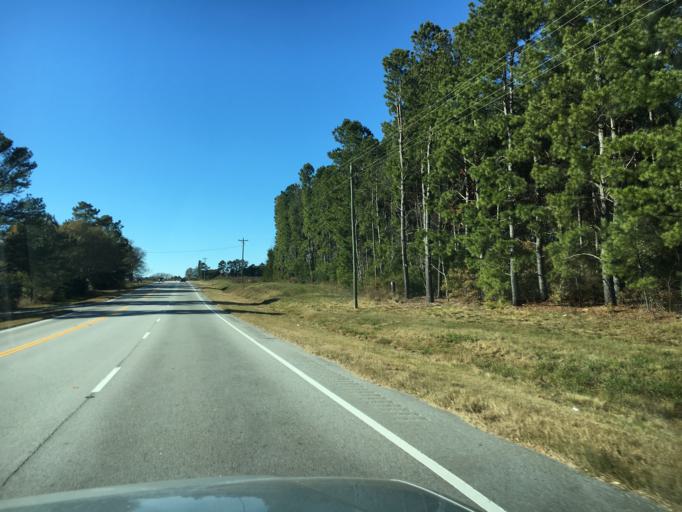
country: US
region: Georgia
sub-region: Hart County
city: Royston
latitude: 34.2935
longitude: -83.0303
